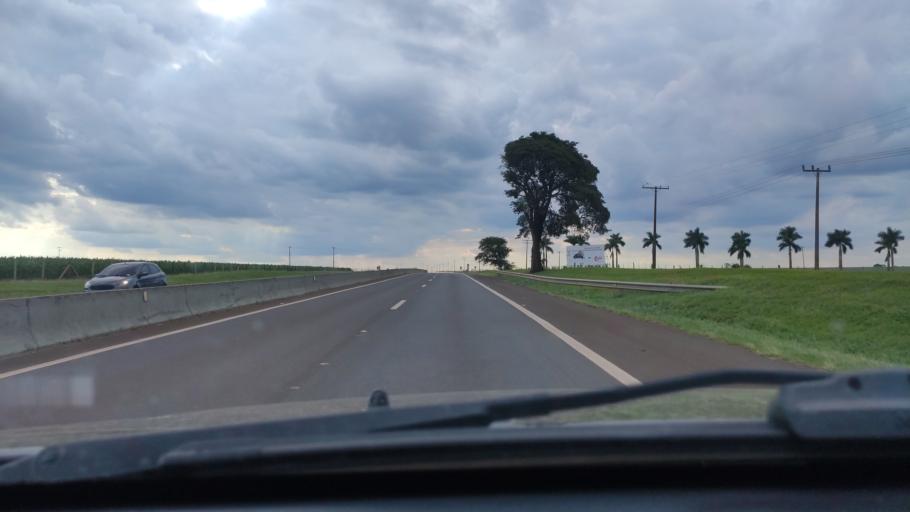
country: BR
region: Sao Paulo
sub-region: Palmital
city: Palmital
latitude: -22.8243
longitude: -50.0370
